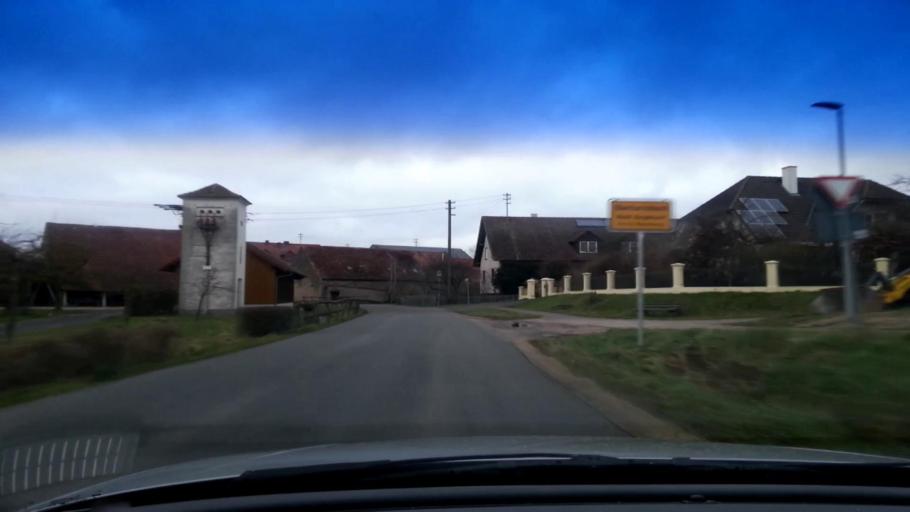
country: DE
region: Bavaria
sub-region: Upper Franconia
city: Walsdorf
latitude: 49.8265
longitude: 10.7902
